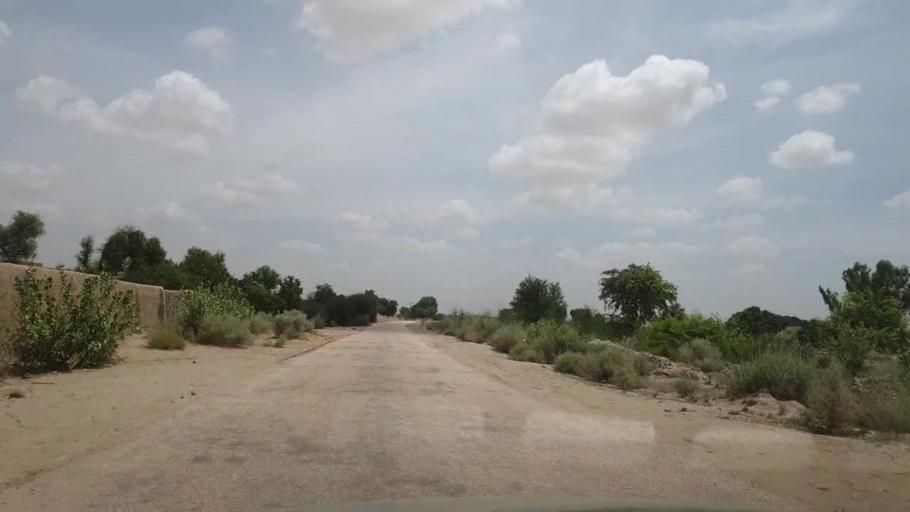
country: PK
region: Sindh
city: Kot Diji
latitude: 27.2095
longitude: 69.1157
